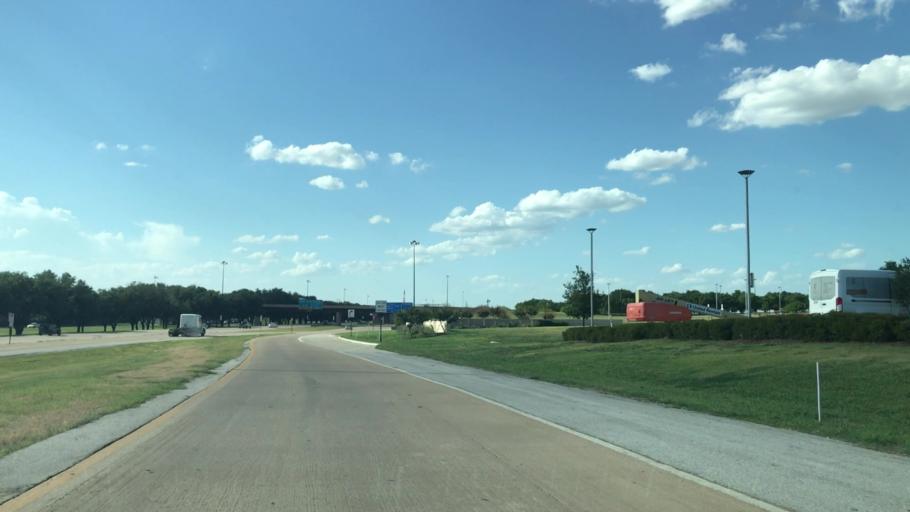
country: US
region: Texas
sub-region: Tarrant County
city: Euless
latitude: 32.8542
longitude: -97.0397
